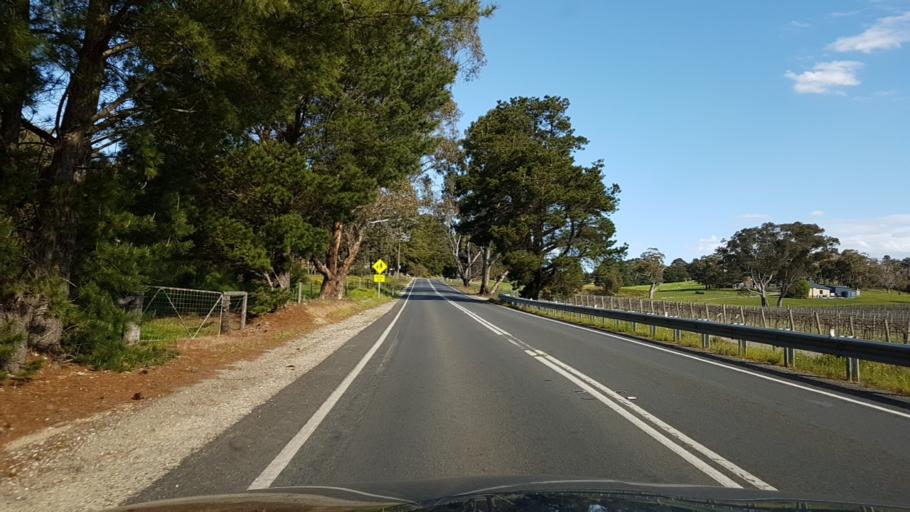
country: AU
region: South Australia
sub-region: Adelaide Hills
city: Lobethal
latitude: -34.8713
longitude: 138.8881
